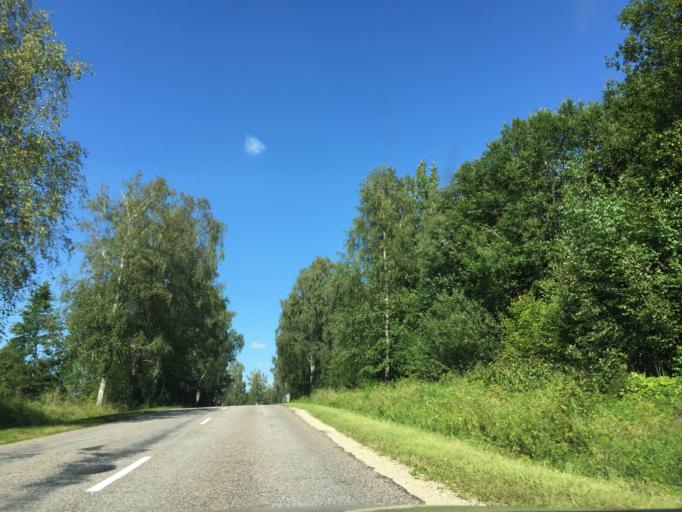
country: LV
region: Limbazu Rajons
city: Limbazi
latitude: 57.4834
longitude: 24.7103
